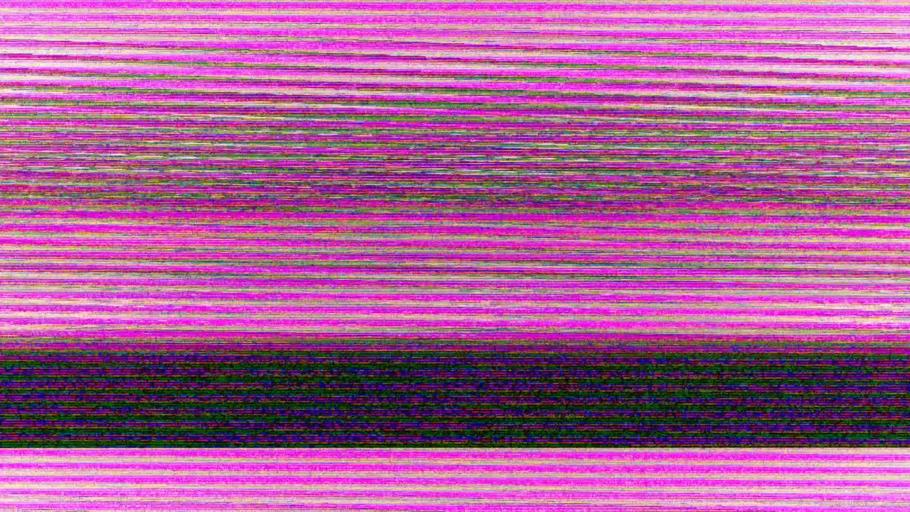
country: US
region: Massachusetts
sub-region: Middlesex County
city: Shirley
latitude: 42.5270
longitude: -71.6306
